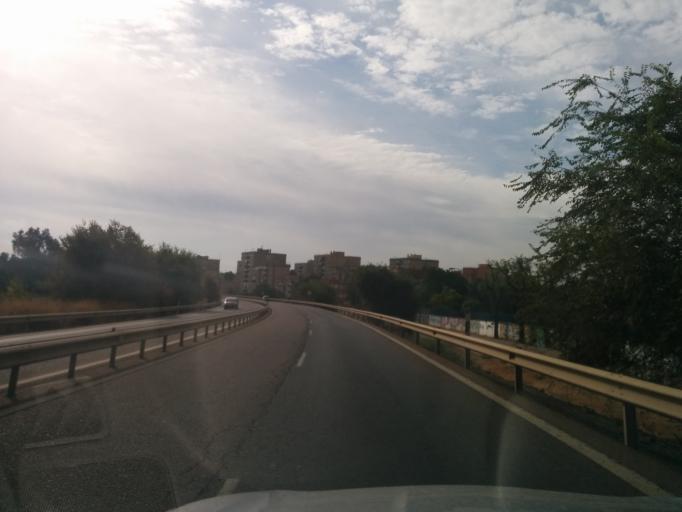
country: ES
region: Andalusia
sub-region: Provincia de Sevilla
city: Sevilla
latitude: 37.4268
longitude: -5.9638
